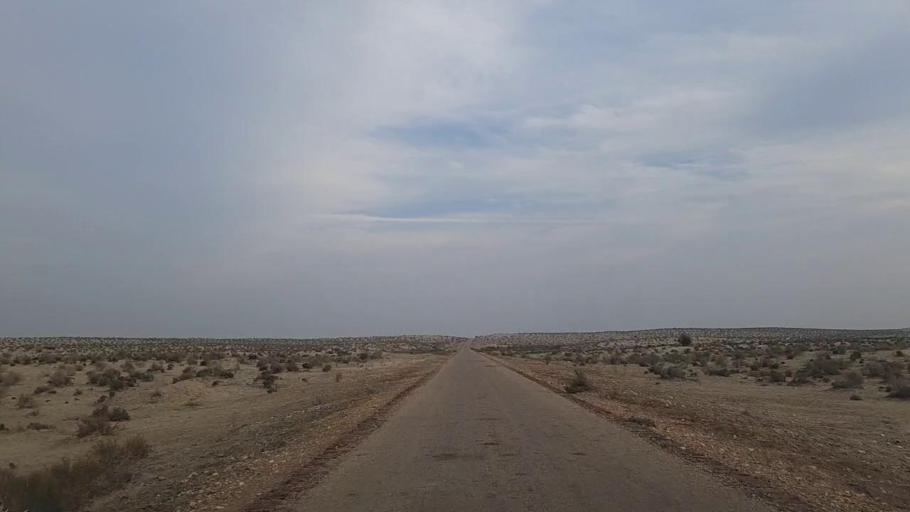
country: PK
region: Sindh
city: Daur
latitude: 26.5120
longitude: 68.5056
